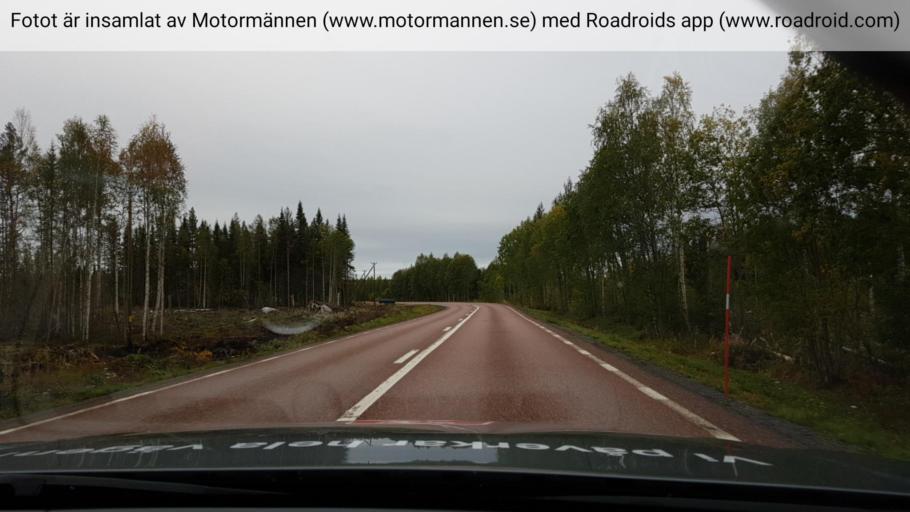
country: SE
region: Jaemtland
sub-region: Stroemsunds Kommun
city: Stroemsund
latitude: 63.9818
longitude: 15.8723
